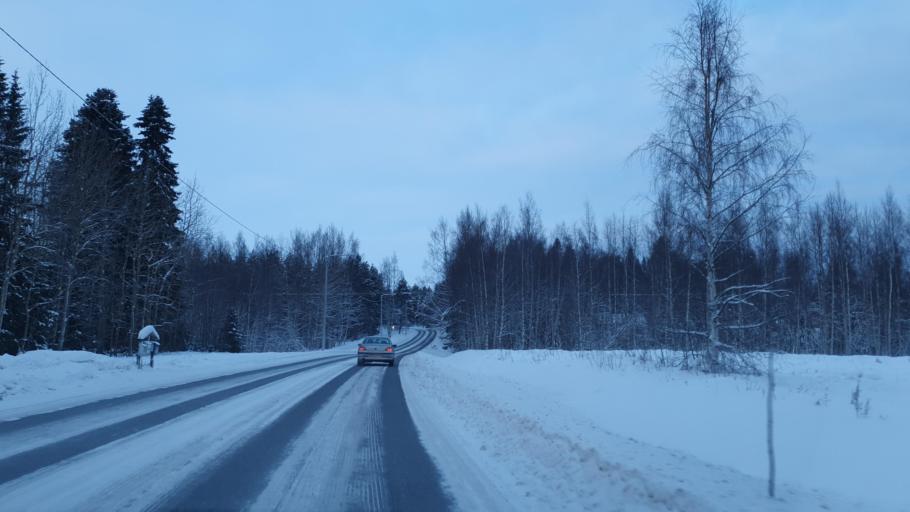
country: FI
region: Northern Ostrobothnia
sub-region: Oulu
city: Haukipudas
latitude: 65.2009
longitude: 25.3397
